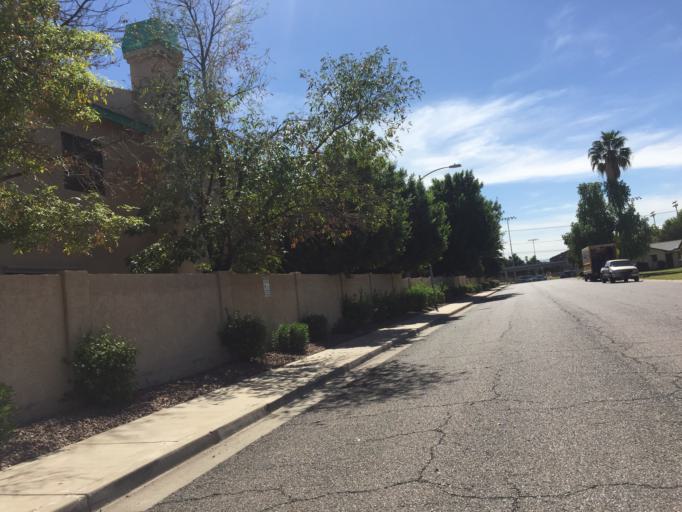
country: US
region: Arizona
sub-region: Maricopa County
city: Phoenix
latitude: 33.5286
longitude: -112.0580
